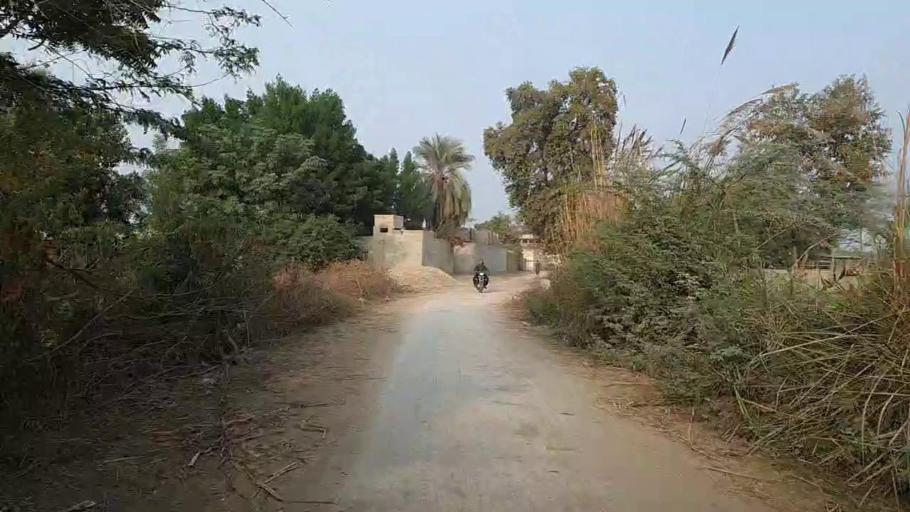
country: PK
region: Sindh
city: Setharja Old
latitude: 27.0970
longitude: 68.5021
